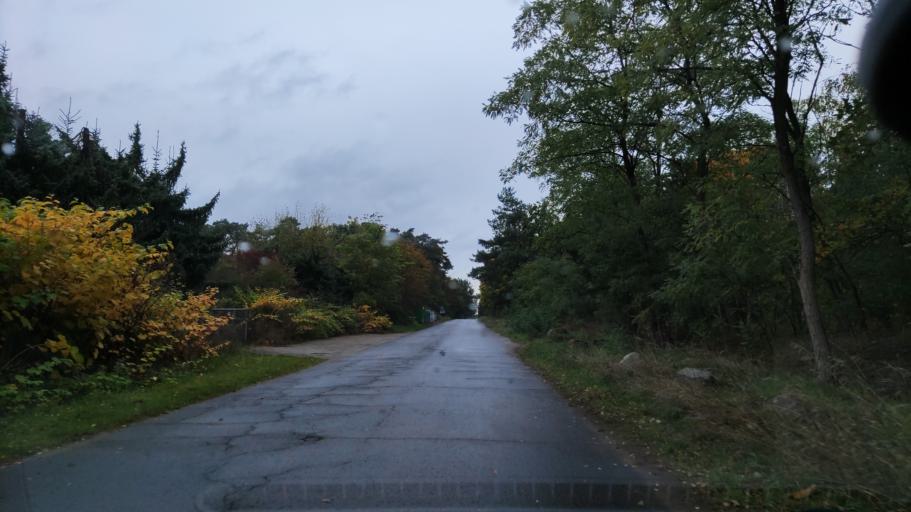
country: DE
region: Lower Saxony
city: Deutsch Evern
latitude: 53.2044
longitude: 10.4492
